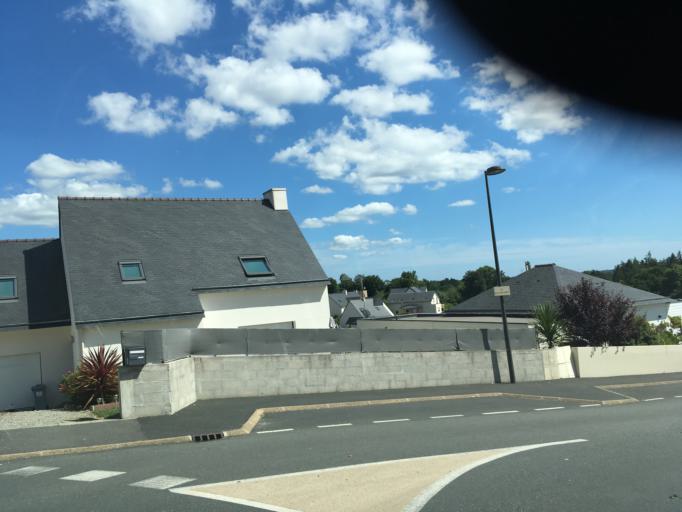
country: FR
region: Brittany
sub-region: Departement du Finistere
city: Ergue-Gaberic
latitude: 47.9818
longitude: -4.0587
